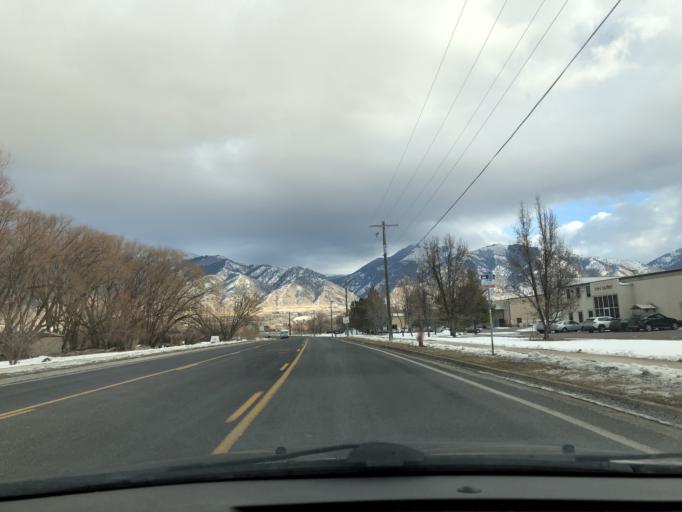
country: US
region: Utah
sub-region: Cache County
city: Providence
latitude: 41.7029
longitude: -111.8475
